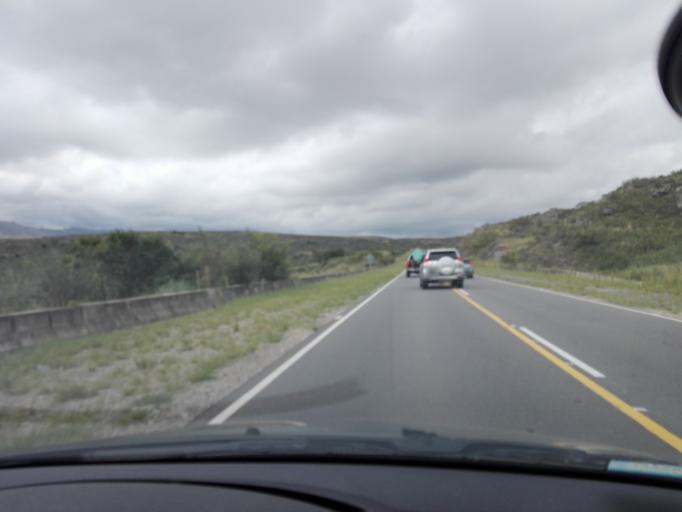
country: AR
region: Cordoba
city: Cuesta Blanca
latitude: -31.5759
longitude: -64.6426
